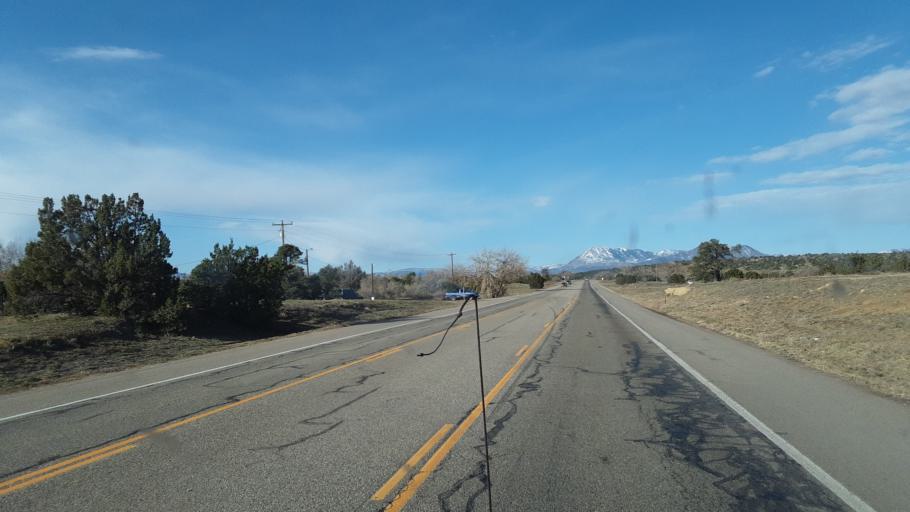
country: US
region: Colorado
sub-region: Huerfano County
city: Walsenburg
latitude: 37.5987
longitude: -104.8467
